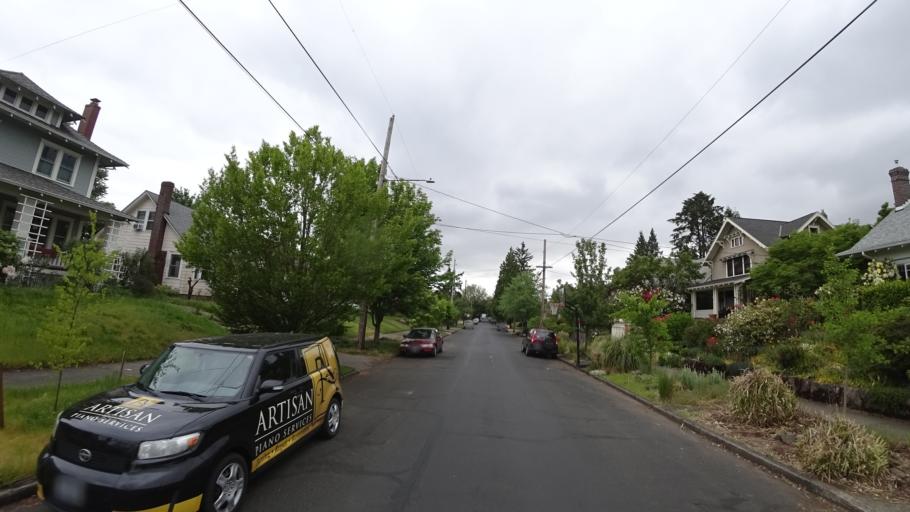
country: US
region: Oregon
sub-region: Multnomah County
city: Portland
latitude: 45.5461
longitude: -122.6188
